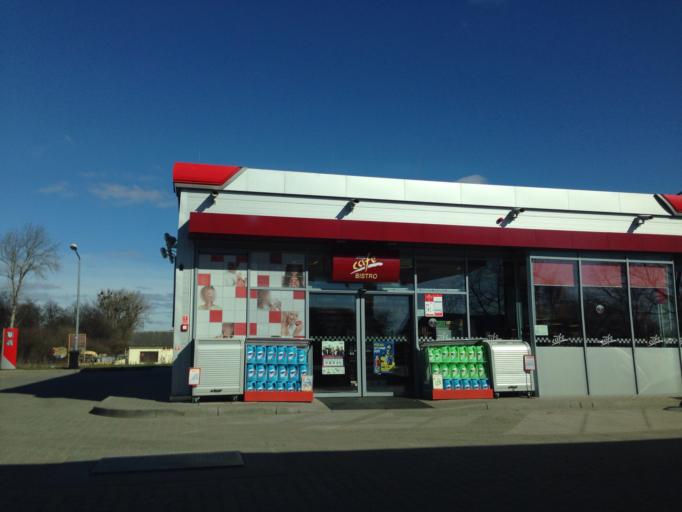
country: PL
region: Pomeranian Voivodeship
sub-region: Powiat tczewski
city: Tczew
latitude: 54.0743
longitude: 18.7771
